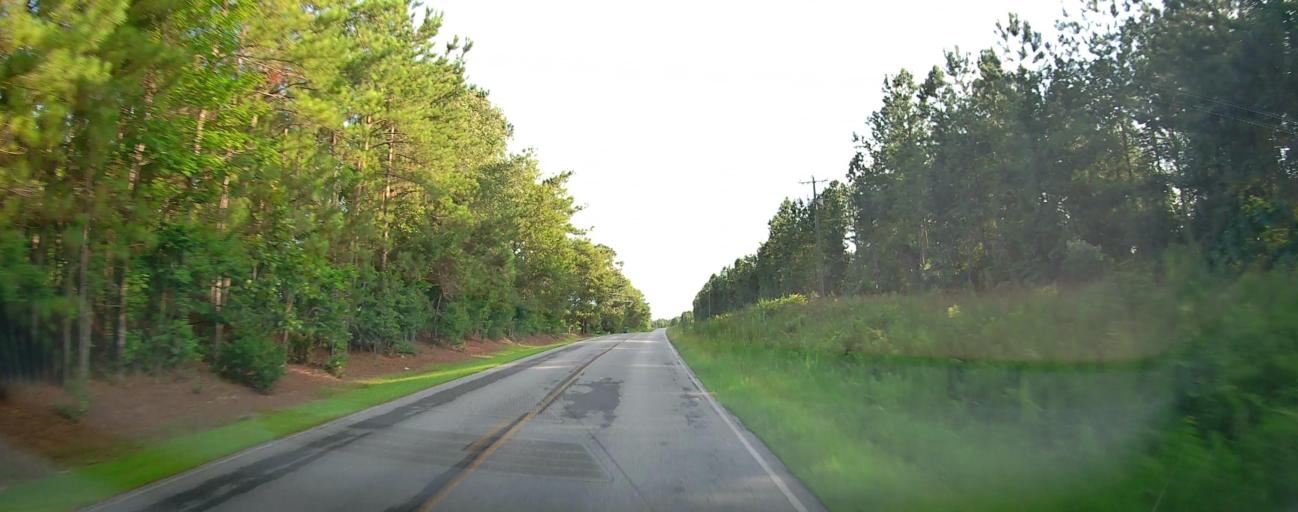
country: US
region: Georgia
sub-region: Bibb County
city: West Point
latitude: 32.7089
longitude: -83.8472
